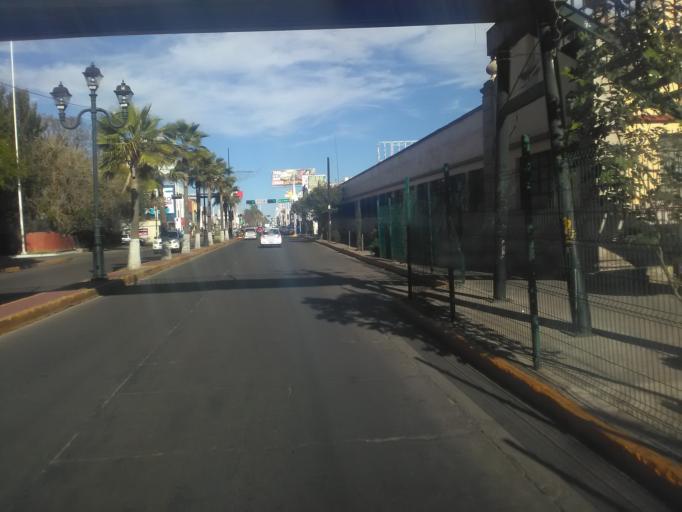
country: MX
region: Durango
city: Victoria de Durango
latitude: 24.0261
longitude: -104.6618
